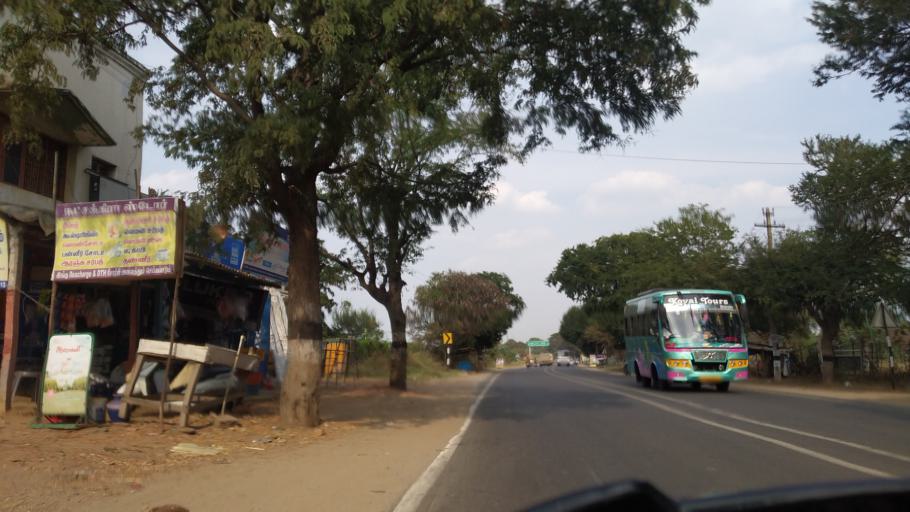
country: IN
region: Tamil Nadu
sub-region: Coimbatore
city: Perur
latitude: 10.9692
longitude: 76.9075
